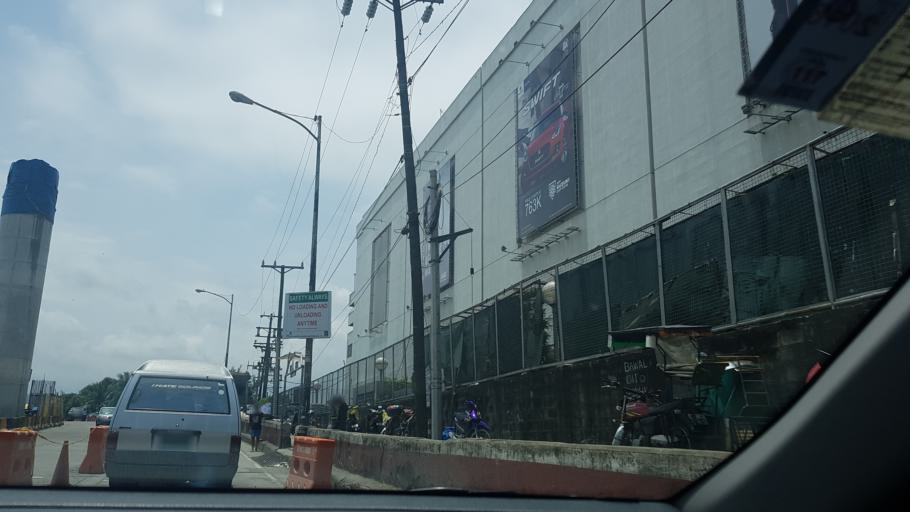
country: PH
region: Metro Manila
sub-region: San Juan
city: San Juan
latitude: 14.6052
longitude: 121.0190
